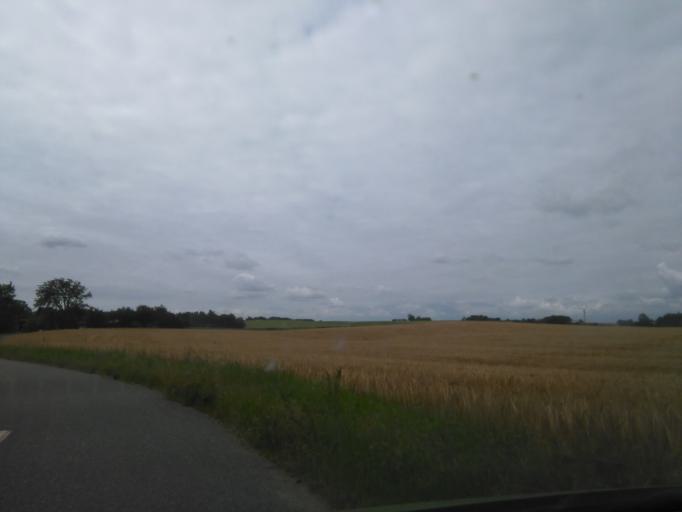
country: DK
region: Central Jutland
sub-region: Arhus Kommune
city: Solbjerg
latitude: 56.0186
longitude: 10.0726
